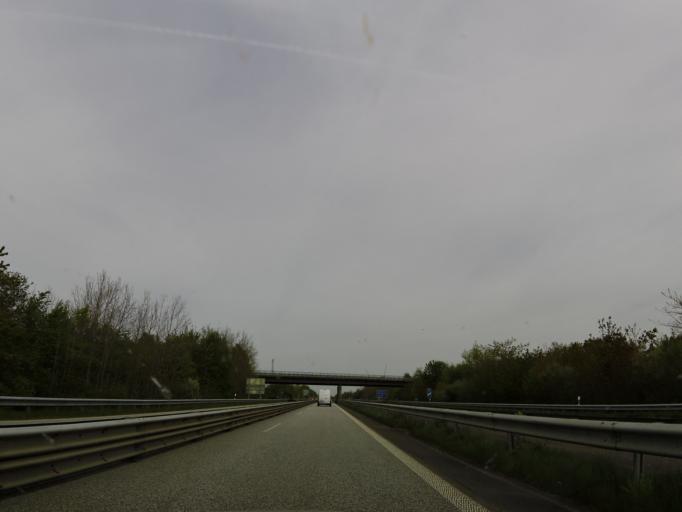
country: DE
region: Schleswig-Holstein
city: Tensbuttel-Rost
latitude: 54.1160
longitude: 9.2599
